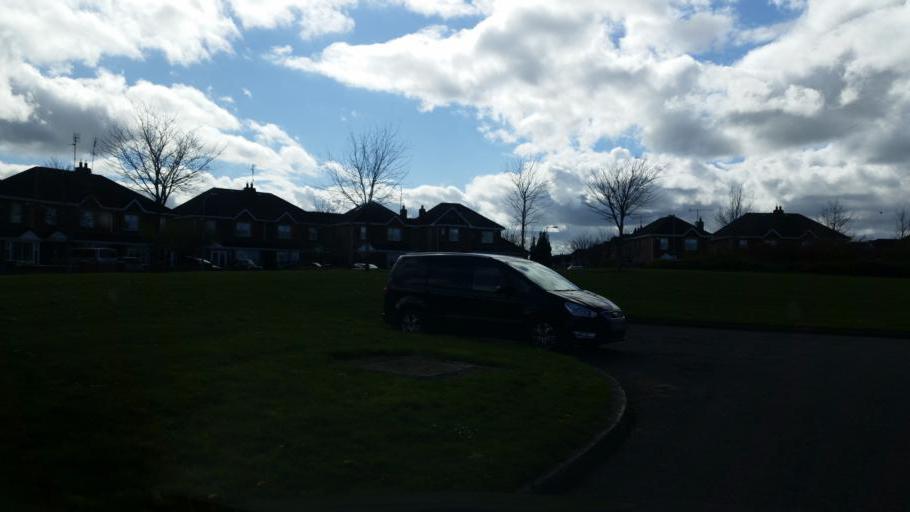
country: IE
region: Leinster
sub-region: Fingal County
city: Swords
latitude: 53.4460
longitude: -6.2320
